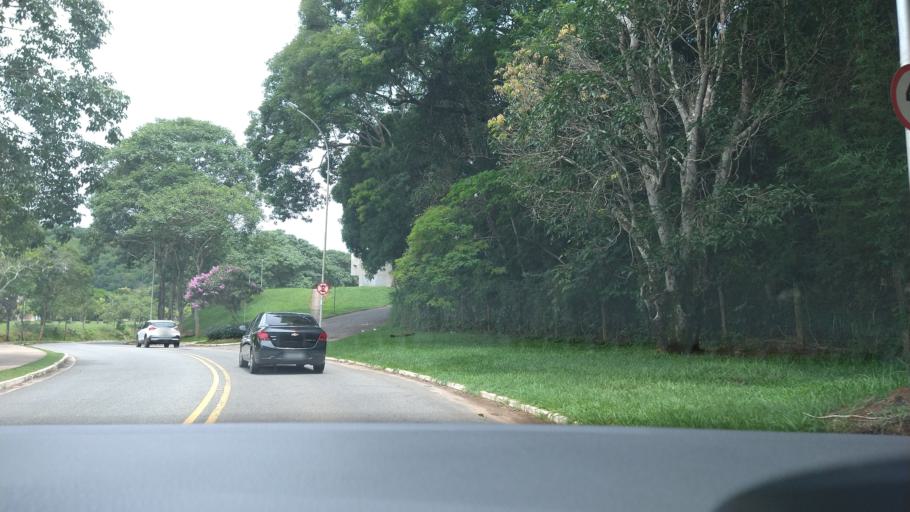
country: BR
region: Minas Gerais
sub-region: Vicosa
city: Vicosa
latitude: -20.7585
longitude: -42.8748
